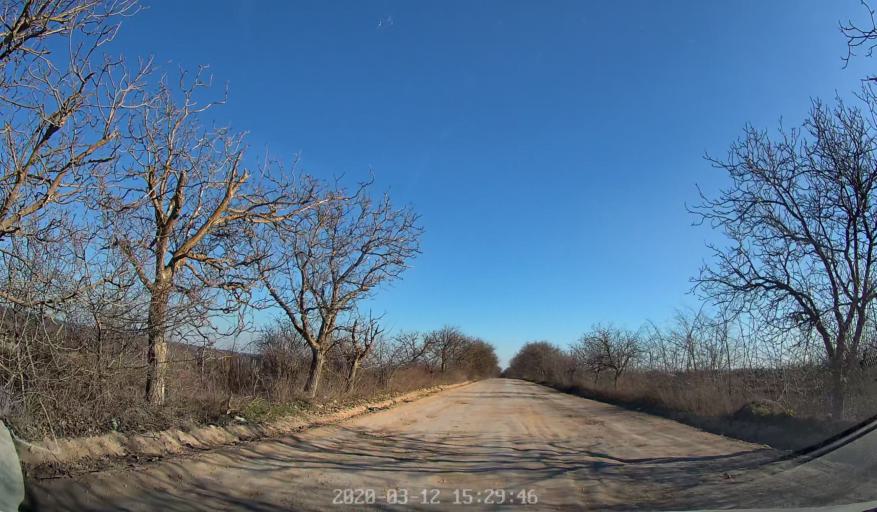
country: MD
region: Chisinau
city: Ciorescu
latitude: 47.1632
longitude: 28.9365
